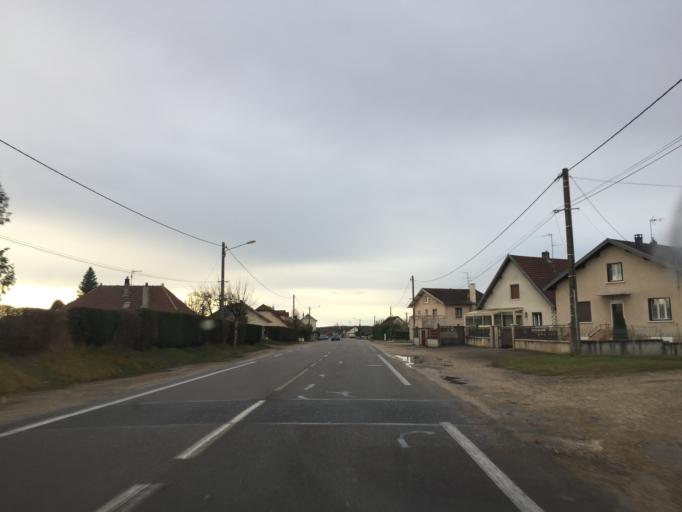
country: FR
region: Franche-Comte
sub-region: Departement du Jura
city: Choisey
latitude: 47.0514
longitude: 5.4941
